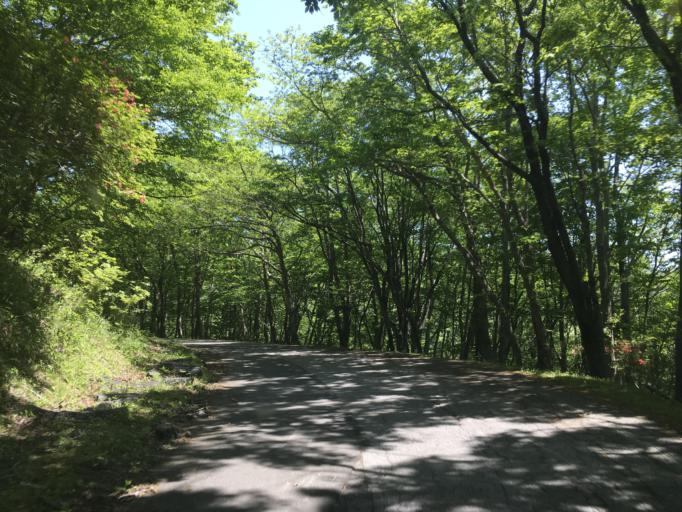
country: JP
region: Iwate
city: Ofunato
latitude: 39.1770
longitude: 141.7300
